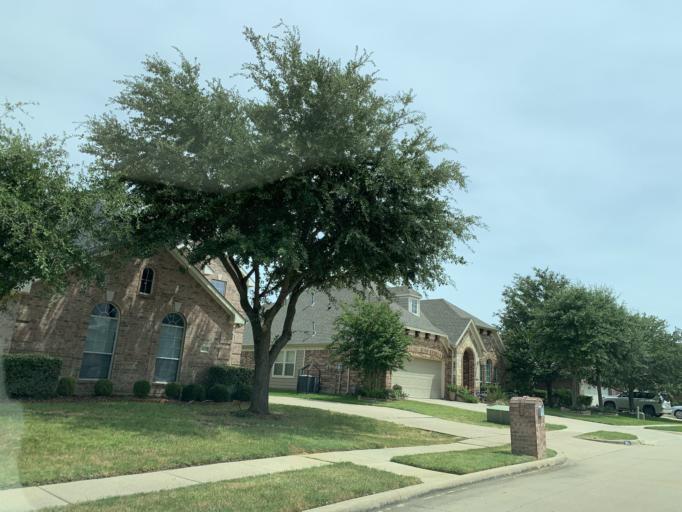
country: US
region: Texas
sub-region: Dallas County
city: Cedar Hill
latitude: 32.6574
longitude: -97.0004
